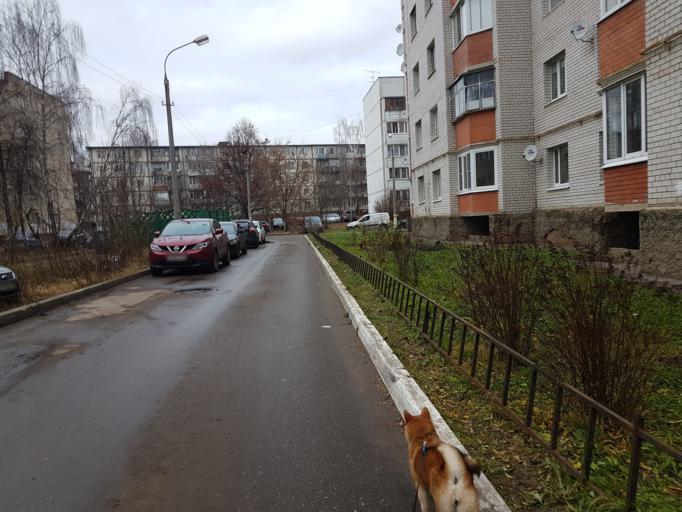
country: RU
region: Moskovskaya
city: Istra
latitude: 55.9084
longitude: 36.8690
